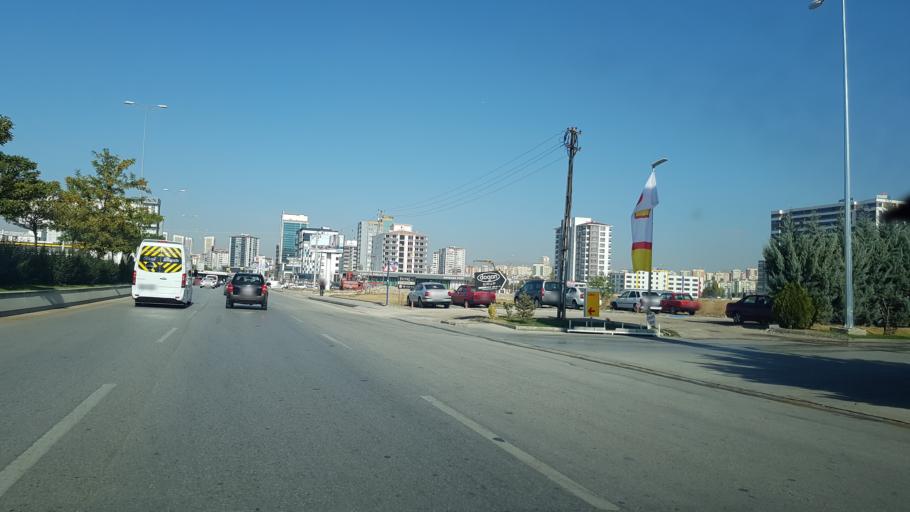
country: TR
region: Ankara
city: Etimesgut
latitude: 39.9628
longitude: 32.6064
